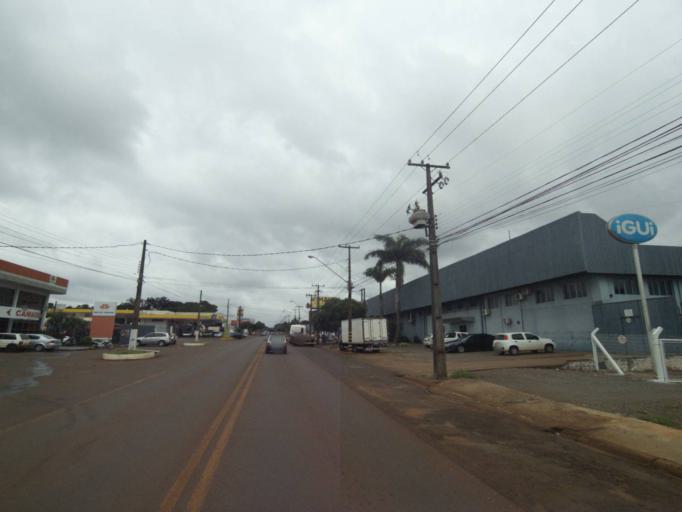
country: BR
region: Parana
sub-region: Campo Mourao
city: Campo Mourao
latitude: -24.0287
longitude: -52.3655
